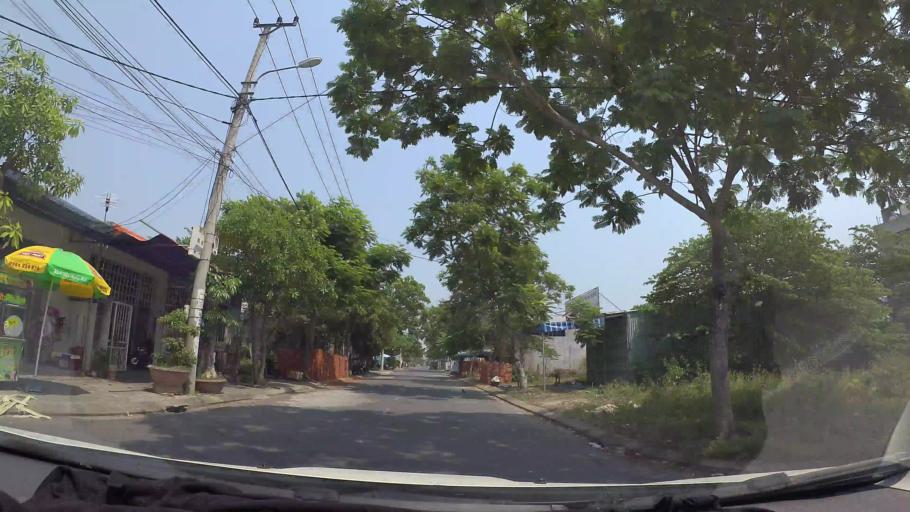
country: VN
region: Da Nang
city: Cam Le
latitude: 15.9957
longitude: 108.1987
